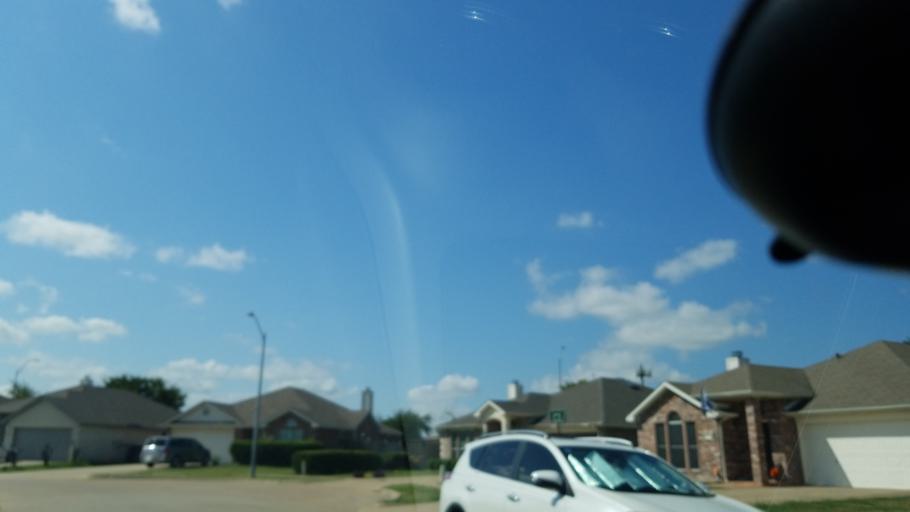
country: US
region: Texas
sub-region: Dallas County
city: Grand Prairie
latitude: 32.7092
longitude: -96.9911
